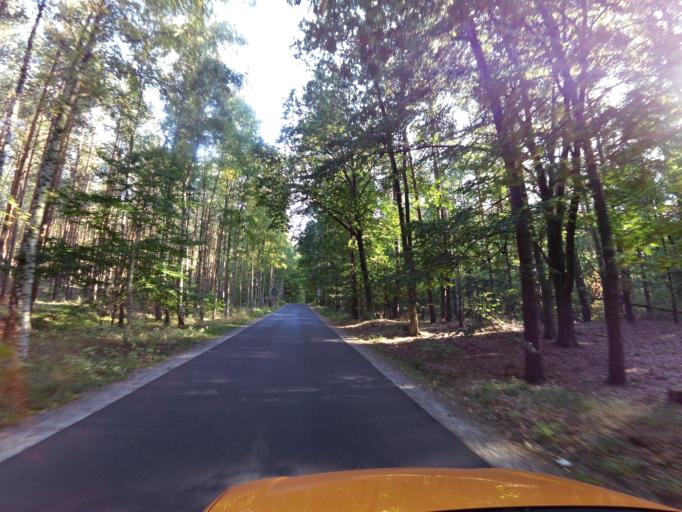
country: DE
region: Brandenburg
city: Potsdam
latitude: 52.4444
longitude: 13.0720
